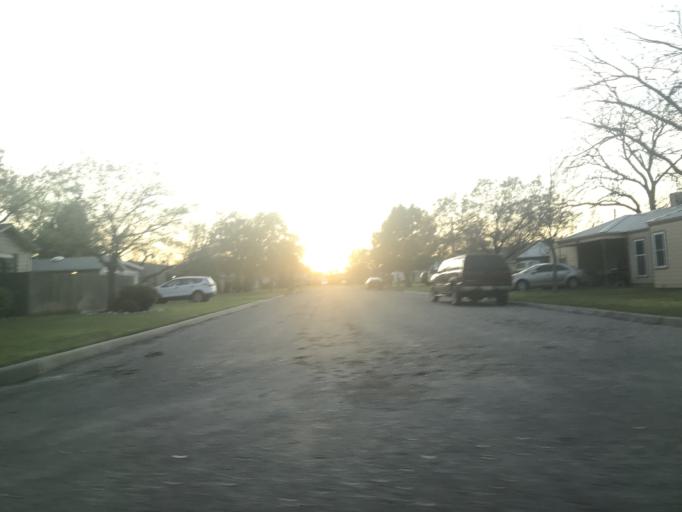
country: US
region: Texas
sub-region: Tom Green County
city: San Angelo
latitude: 31.4462
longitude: -100.4573
